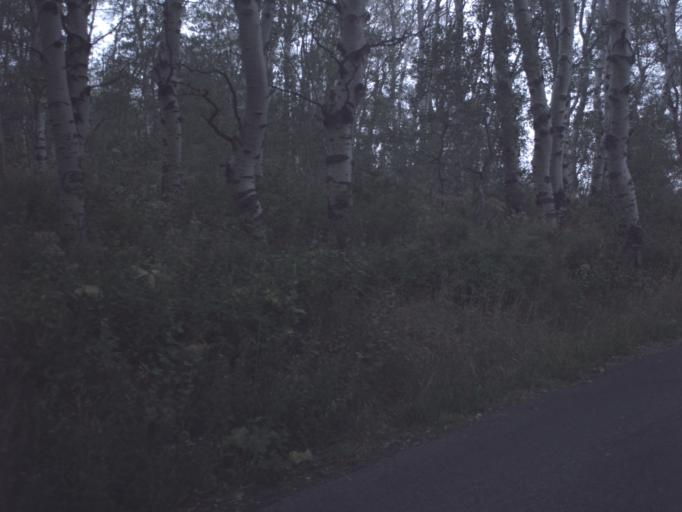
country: US
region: Utah
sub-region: Utah County
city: Lindon
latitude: 40.4267
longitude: -111.6075
